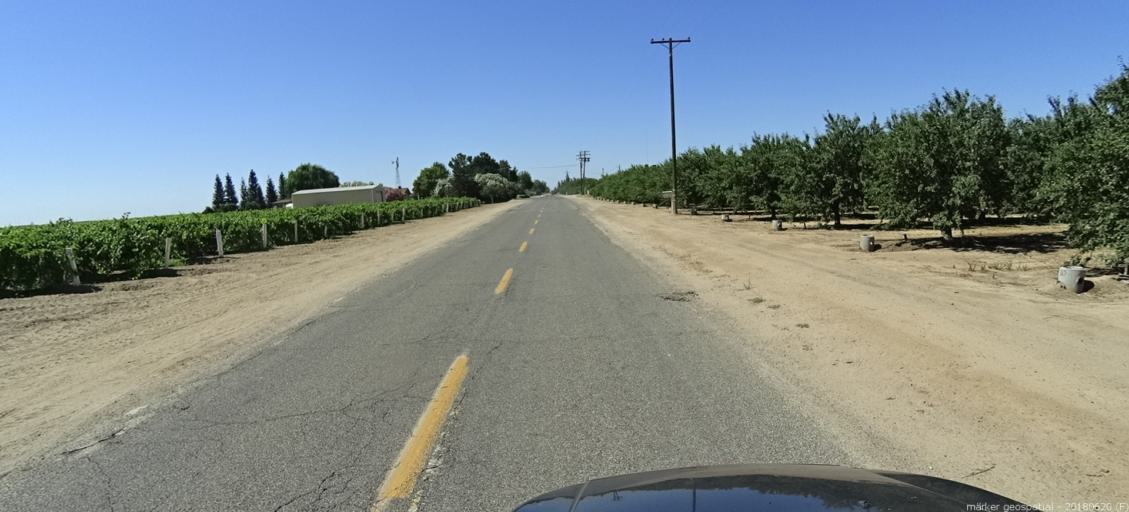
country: US
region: California
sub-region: Madera County
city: Parkwood
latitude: 36.8980
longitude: -120.0195
